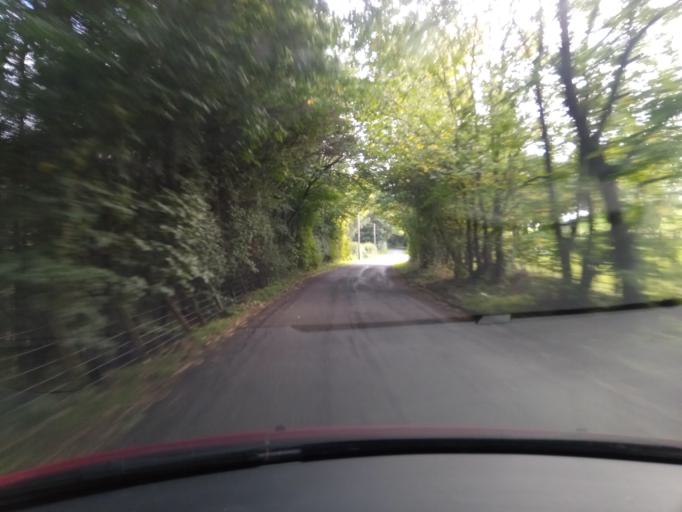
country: GB
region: Scotland
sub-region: The Scottish Borders
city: Kelso
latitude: 55.5006
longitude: -2.3477
